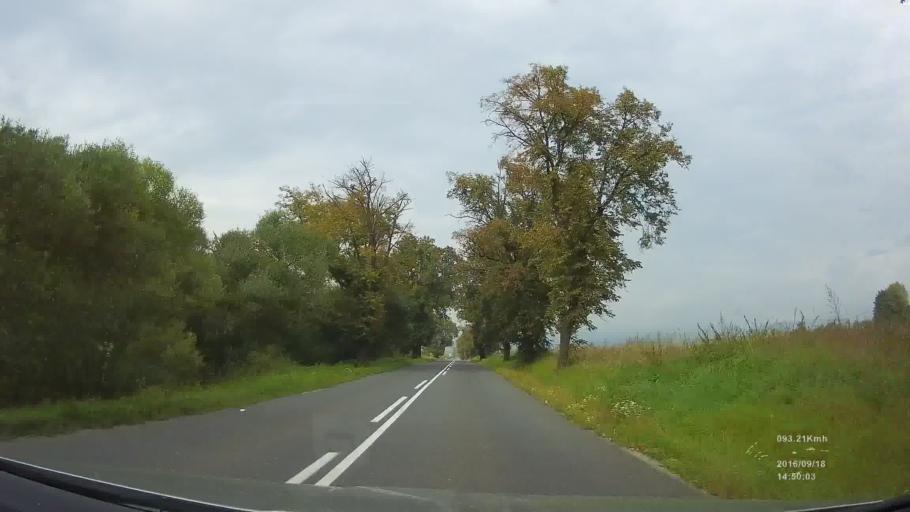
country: SK
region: Presovsky
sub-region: Okres Presov
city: Levoca
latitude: 48.9915
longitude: 20.5812
